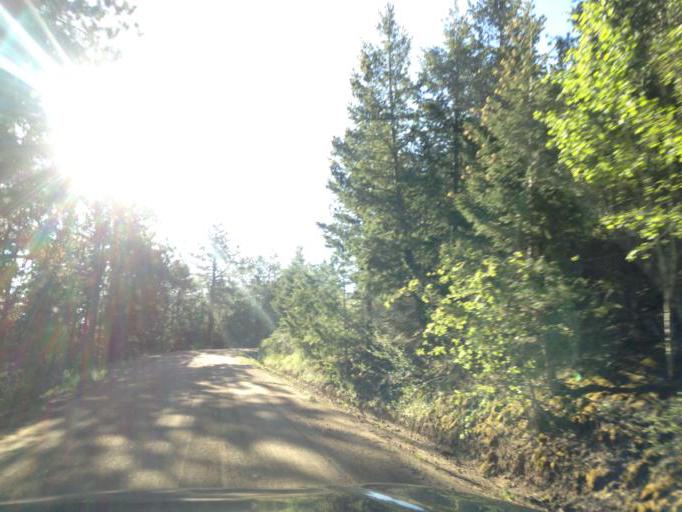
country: US
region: Colorado
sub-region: Jefferson County
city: Evergreen
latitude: 39.4087
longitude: -105.5247
